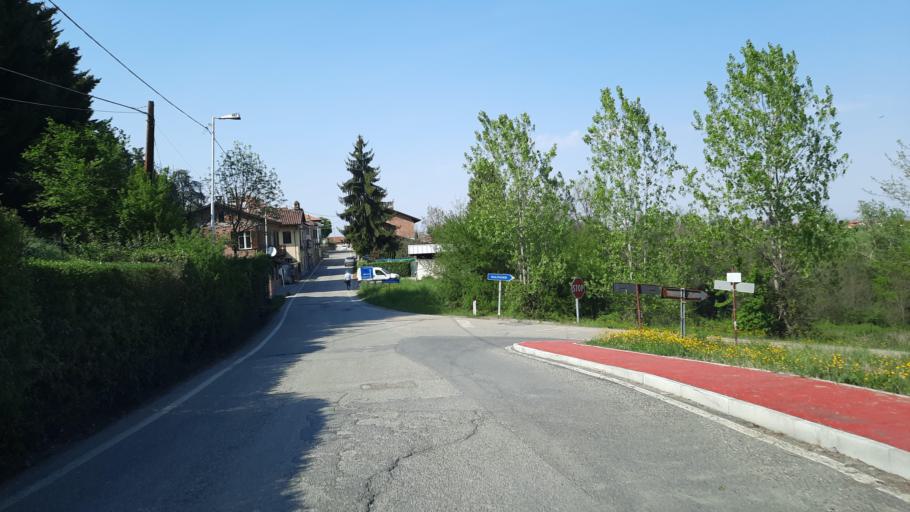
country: IT
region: Piedmont
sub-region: Provincia di Torino
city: Valentino
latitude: 45.1548
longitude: 8.0939
